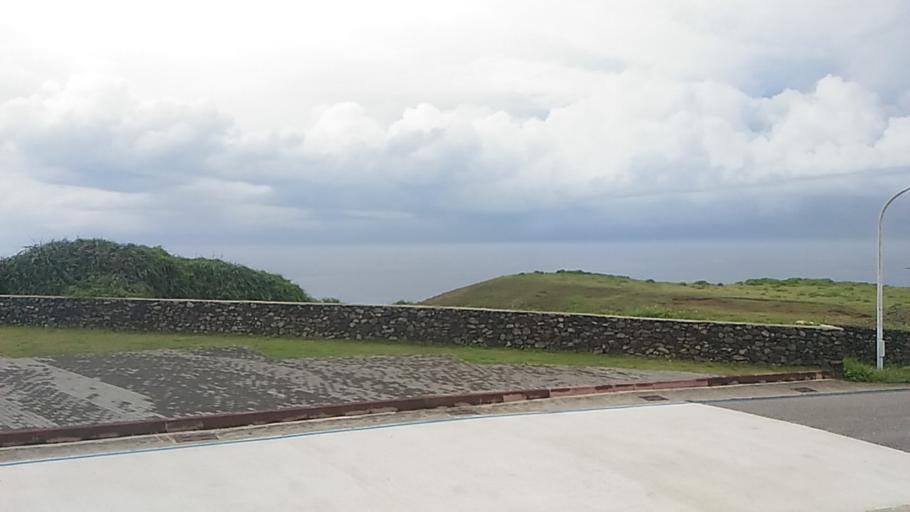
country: TW
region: Taiwan
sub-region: Penghu
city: Ma-kung
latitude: 23.2020
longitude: 119.4344
